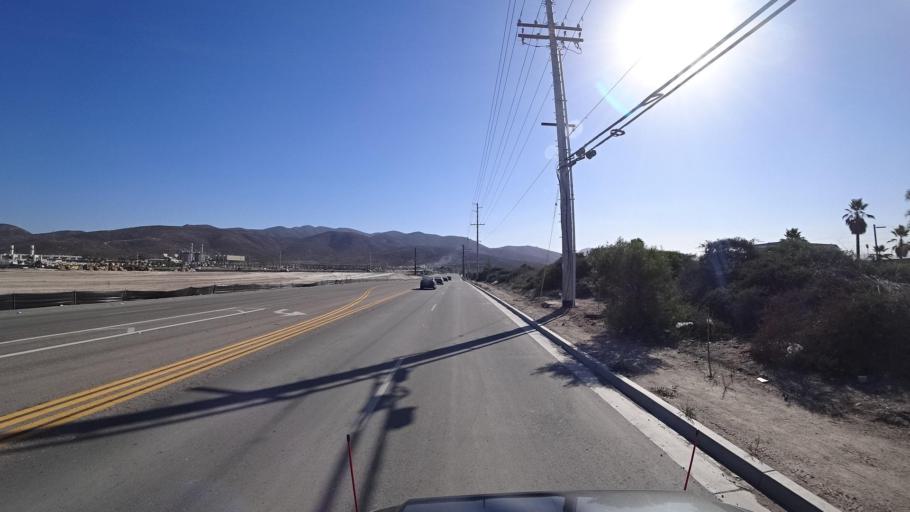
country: MX
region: Baja California
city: Tijuana
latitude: 32.5674
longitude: -116.9224
